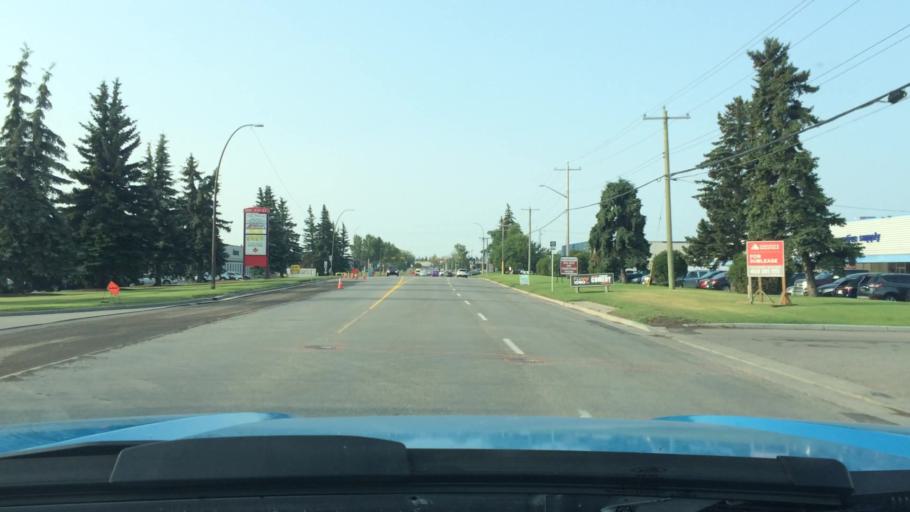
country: CA
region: Alberta
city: Calgary
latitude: 51.0840
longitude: -114.0117
